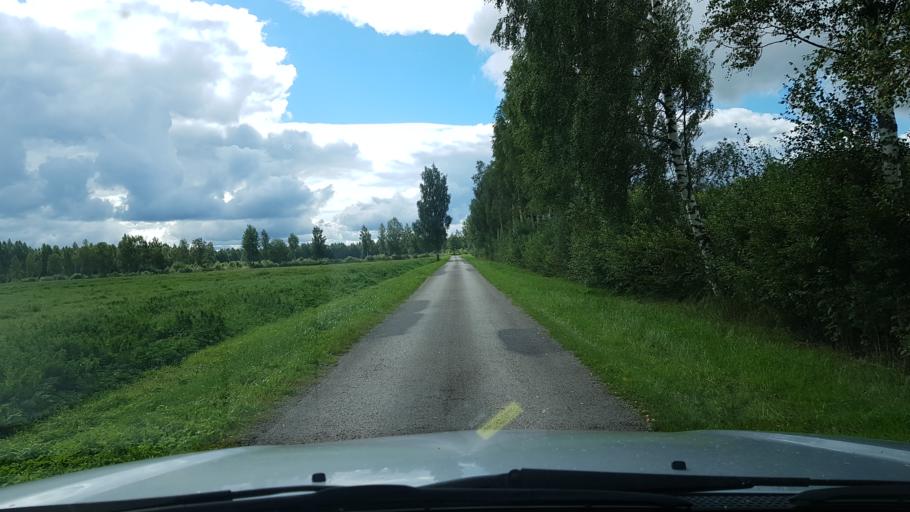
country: EE
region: Harju
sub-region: Raasiku vald
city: Arukula
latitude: 59.2990
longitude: 25.0571
